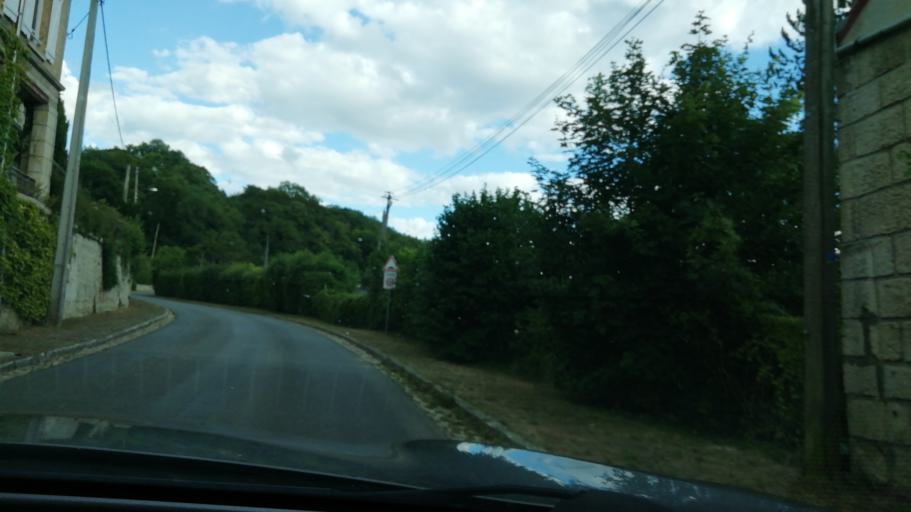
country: FR
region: Picardie
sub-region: Departement de l'Oise
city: Pierrefonds
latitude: 49.3471
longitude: 2.9838
